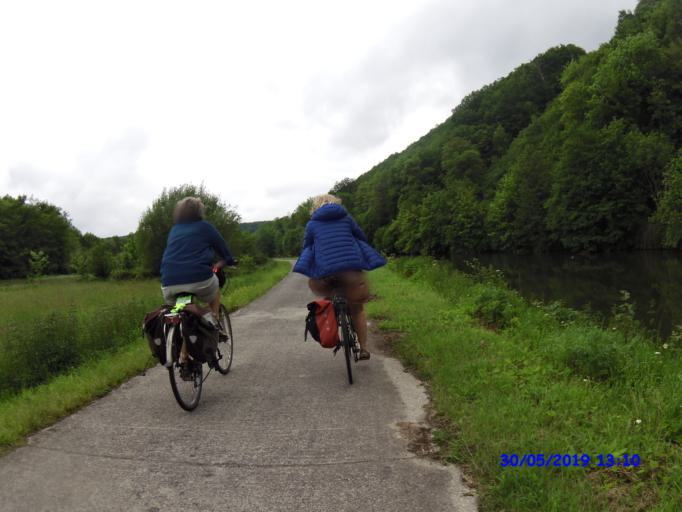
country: BE
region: Wallonia
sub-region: Province du Hainaut
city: Thuin
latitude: 50.3619
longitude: 4.3142
